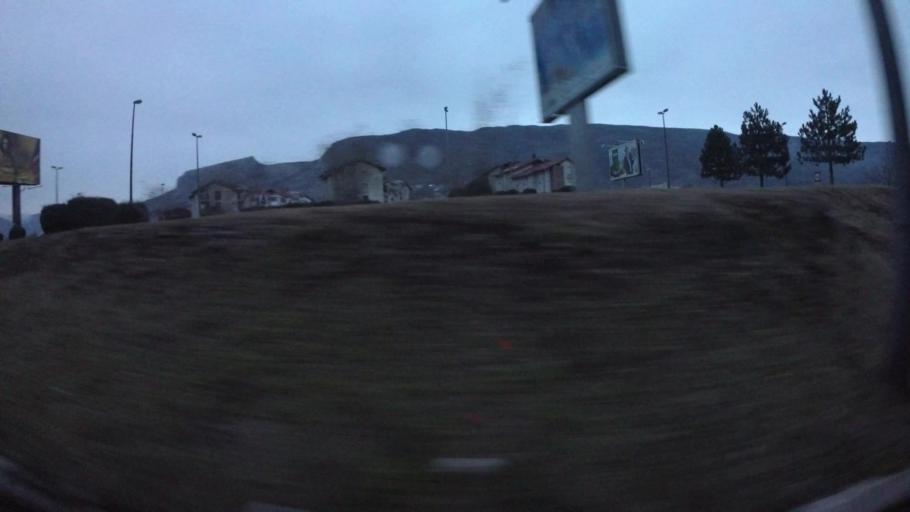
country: BA
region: Federation of Bosnia and Herzegovina
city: Rodoc
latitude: 43.3265
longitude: 17.8165
